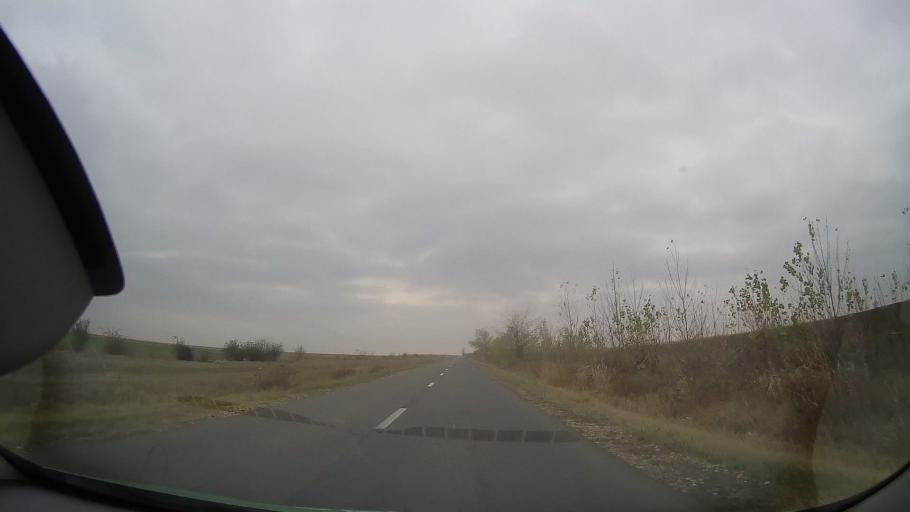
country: RO
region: Ialomita
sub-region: Comuna Garbovi
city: Garbovi
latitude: 44.7711
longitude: 26.7441
